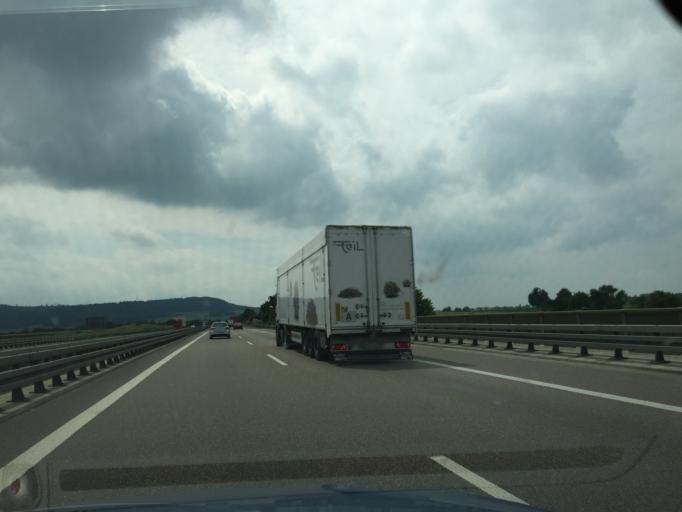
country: DE
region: Baden-Wuerttemberg
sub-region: Regierungsbezirk Stuttgart
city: Westhausen
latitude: 48.8978
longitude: 10.1775
